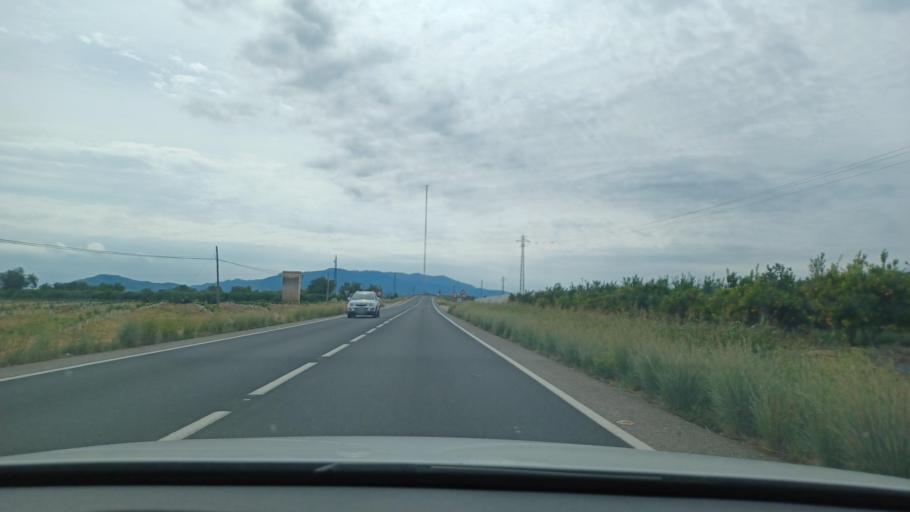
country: ES
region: Catalonia
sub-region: Provincia de Tarragona
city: Santa Barbara
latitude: 40.7426
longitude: 0.5040
